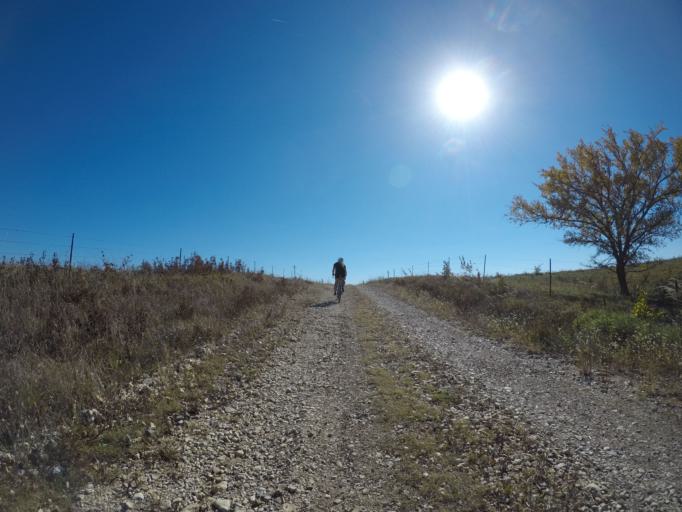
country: US
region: Kansas
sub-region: Wabaunsee County
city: Alma
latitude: 38.9741
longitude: -96.4554
